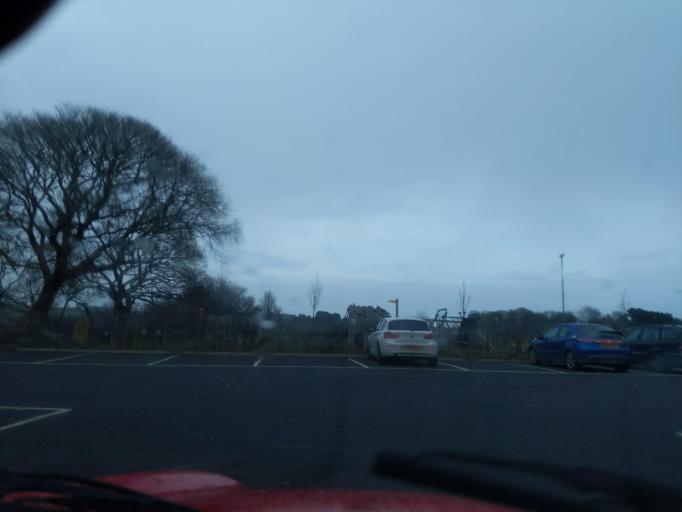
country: GB
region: England
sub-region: Devon
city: Wembury
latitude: 50.3266
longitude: -4.0698
